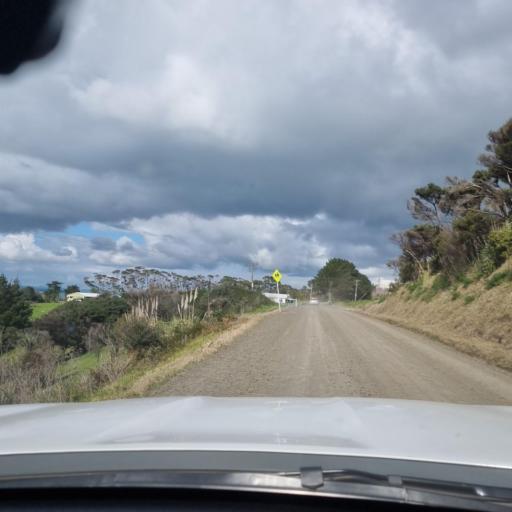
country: NZ
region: Auckland
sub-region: Auckland
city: Wellsford
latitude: -36.3518
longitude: 174.1720
